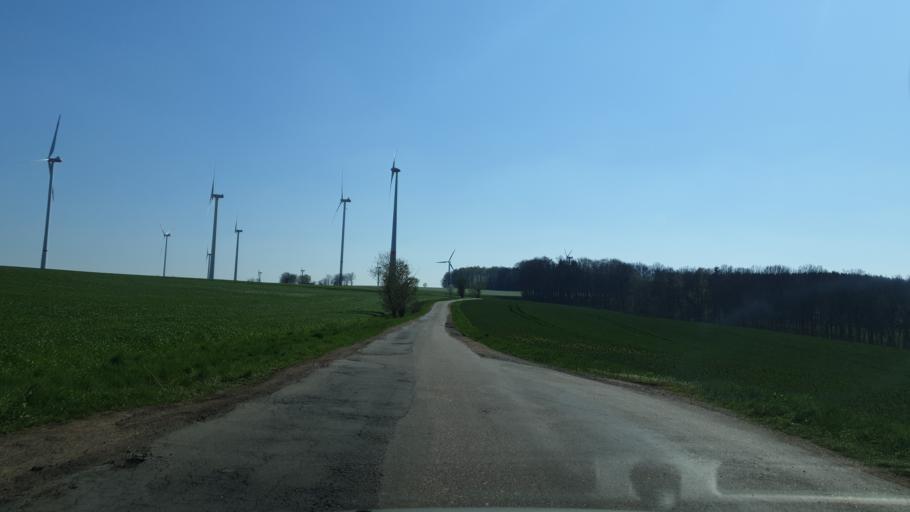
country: DE
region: Saxony
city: Bernsdorf
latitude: 50.7735
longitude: 12.6848
